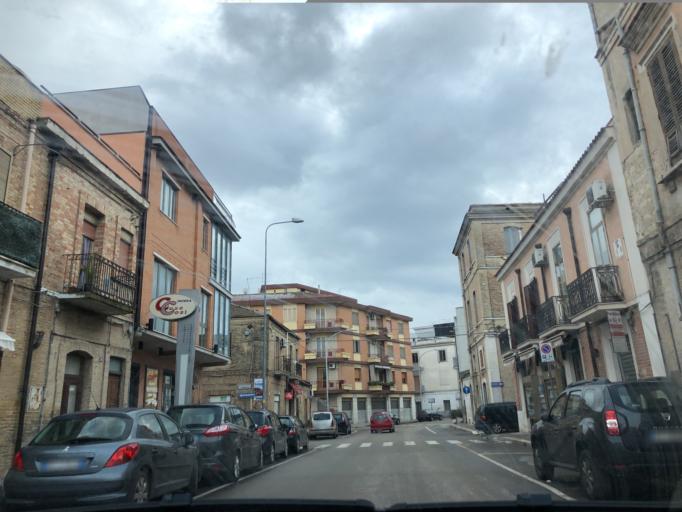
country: IT
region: Apulia
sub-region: Provincia di Foggia
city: Lucera
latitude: 41.5078
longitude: 15.3402
